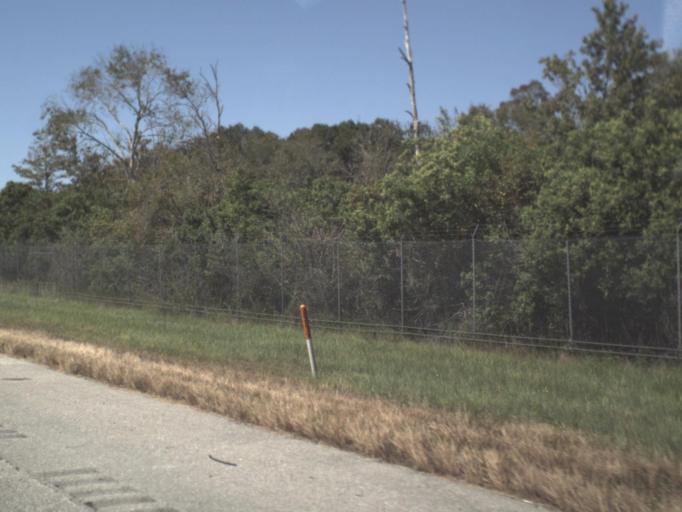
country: US
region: Florida
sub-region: Collier County
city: Orangetree
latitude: 26.1533
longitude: -81.5116
